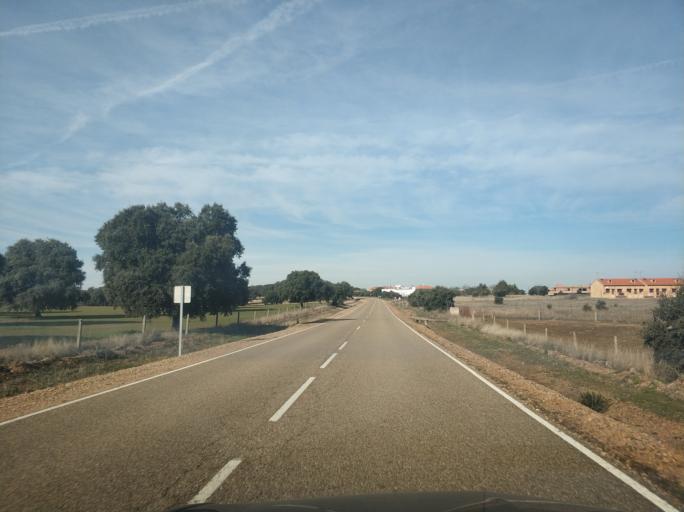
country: ES
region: Castille and Leon
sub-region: Provincia de Salamanca
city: Zarapicos
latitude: 41.0077
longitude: -5.8406
